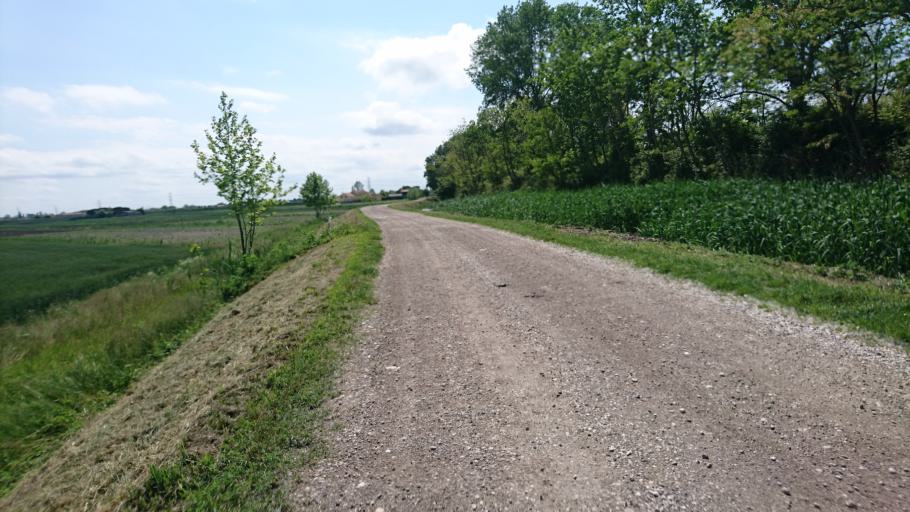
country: IT
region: Veneto
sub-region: Provincia di Padova
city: Codevigo
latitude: 45.2584
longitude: 12.1386
